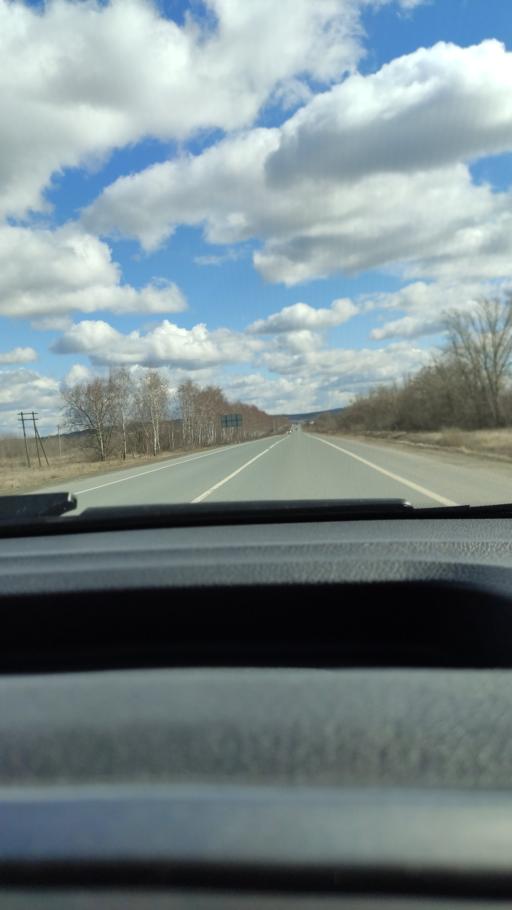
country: RU
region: Samara
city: Kurumoch
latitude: 53.4885
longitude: 49.9953
